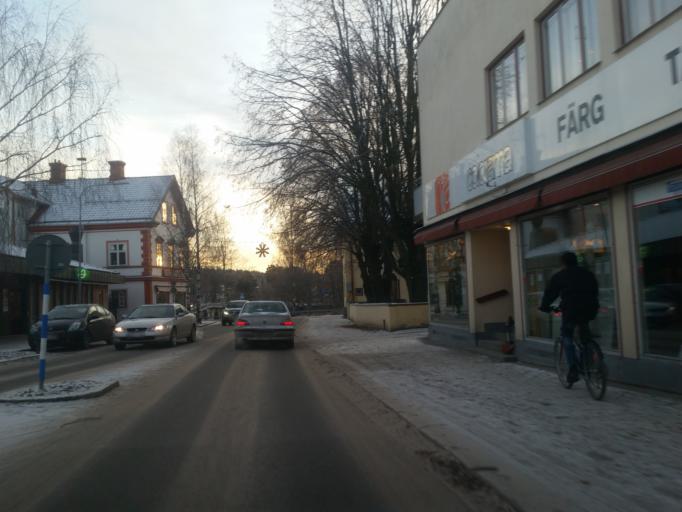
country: SE
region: Dalarna
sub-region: Leksand Municipality
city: Leksand
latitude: 60.7309
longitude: 14.9974
